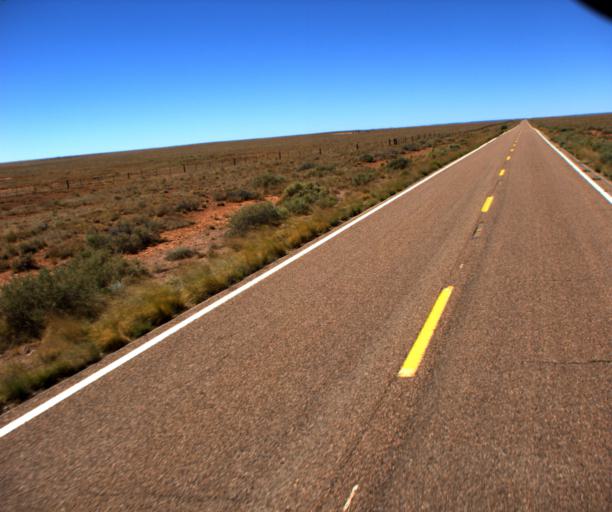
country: US
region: Arizona
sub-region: Navajo County
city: Winslow
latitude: 34.8925
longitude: -110.6470
